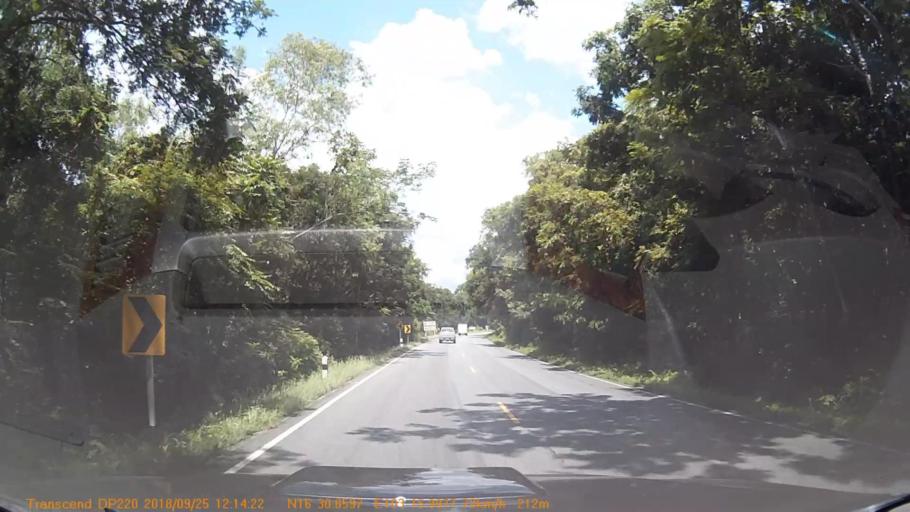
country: TH
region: Kalasin
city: Huai Mek
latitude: 16.5145
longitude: 103.2666
